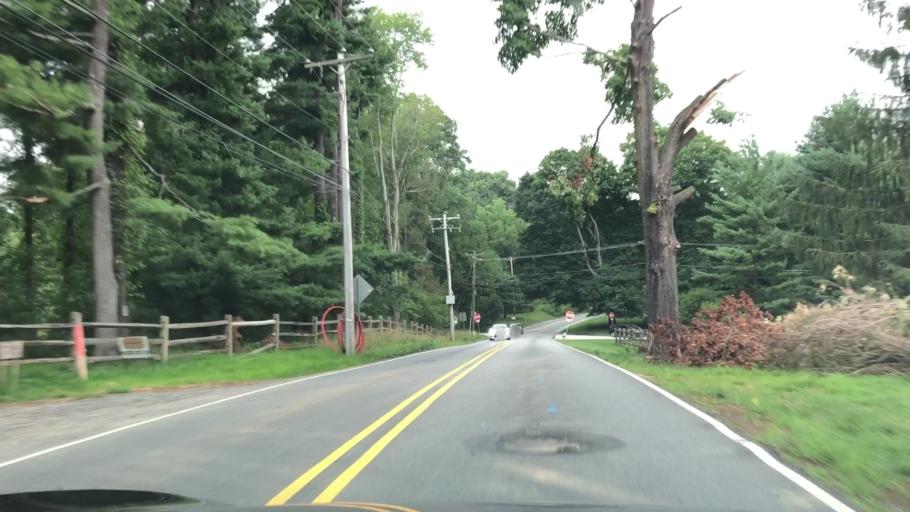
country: US
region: Pennsylvania
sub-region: Chester County
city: Devon
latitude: 40.0265
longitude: -75.4180
